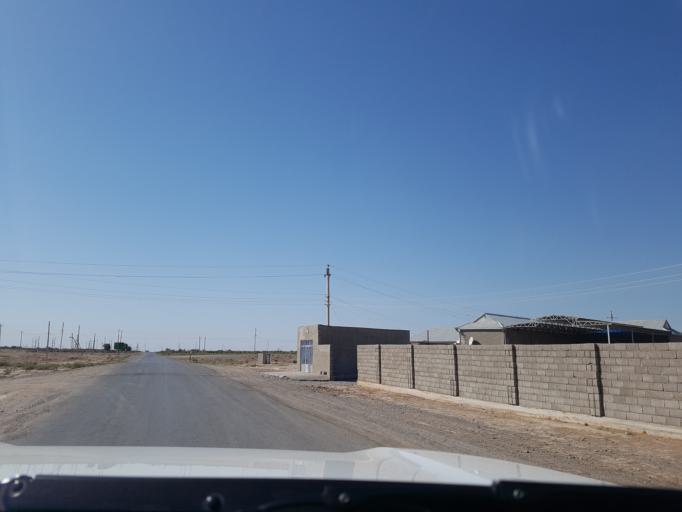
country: IR
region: Razavi Khorasan
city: Sarakhs
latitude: 36.5202
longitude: 61.2505
